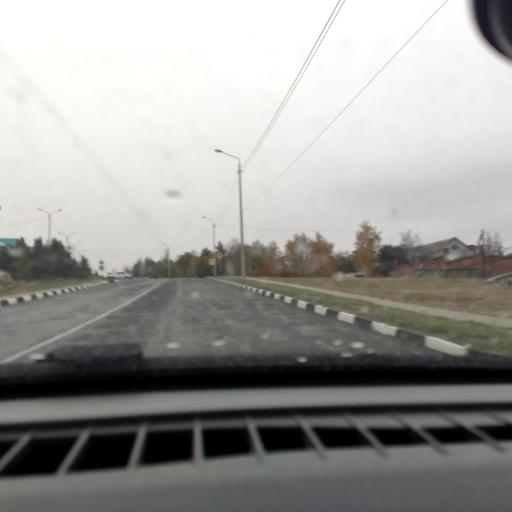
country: RU
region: Belgorod
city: Alekseyevka
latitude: 50.6425
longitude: 38.6910
